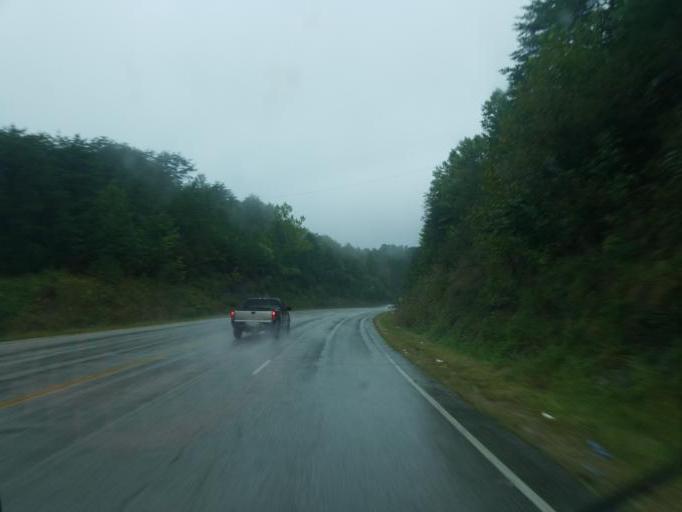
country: US
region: Kentucky
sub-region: Carter County
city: Olive Hill
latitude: 38.3234
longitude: -83.2058
